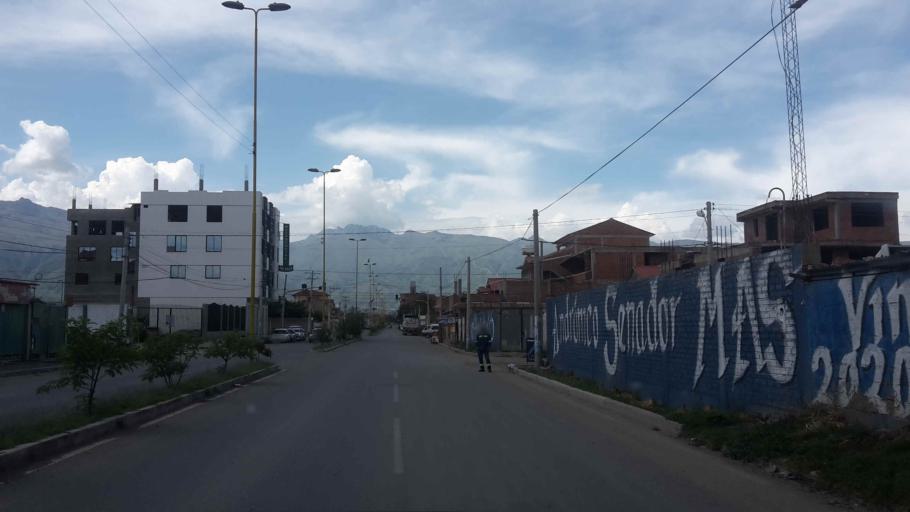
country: BO
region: Cochabamba
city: Sipe Sipe
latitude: -17.4081
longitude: -66.2863
